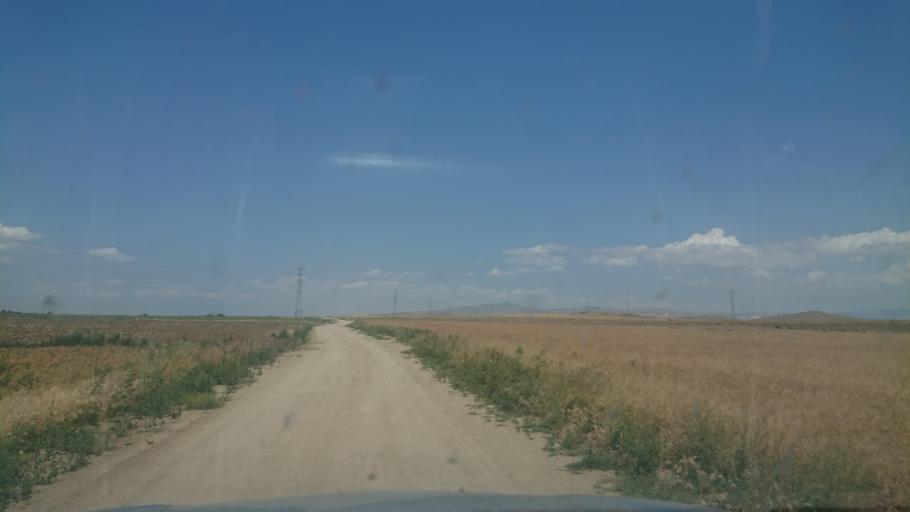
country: TR
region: Aksaray
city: Sariyahsi
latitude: 39.0086
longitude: 33.8823
